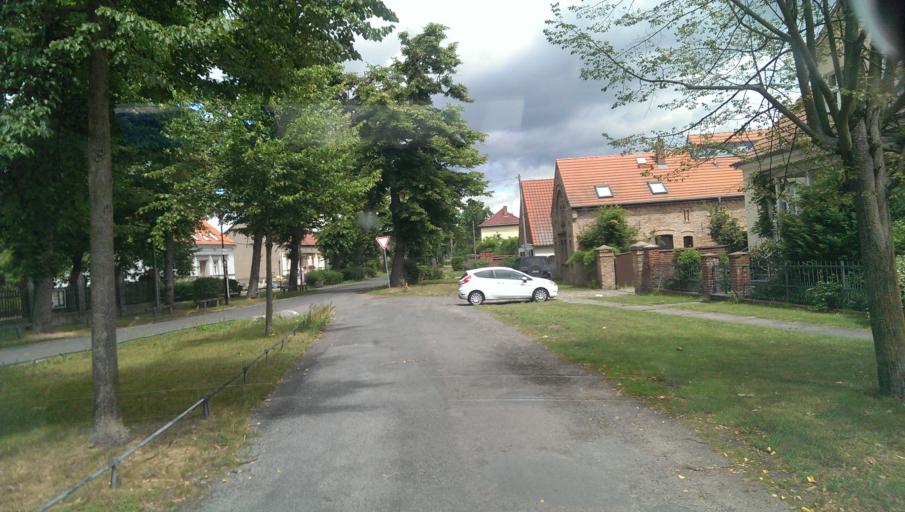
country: DE
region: Brandenburg
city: Ludwigsfelde
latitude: 52.2841
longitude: 13.1682
